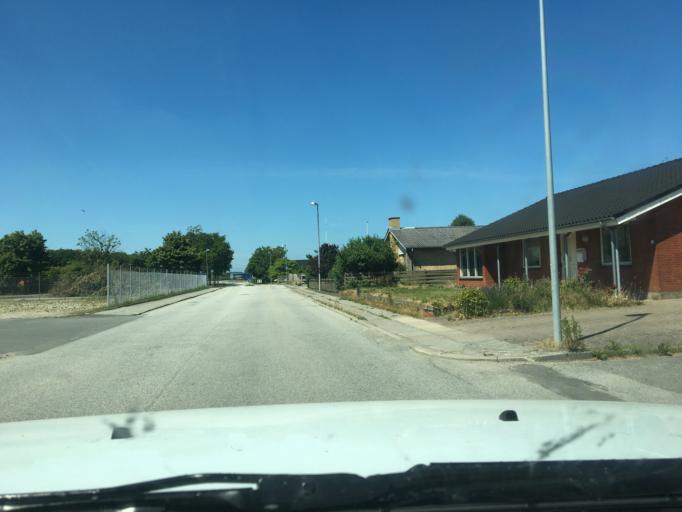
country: DK
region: Central Jutland
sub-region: Horsens Kommune
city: Braedstrup
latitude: 55.9719
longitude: 9.6073
